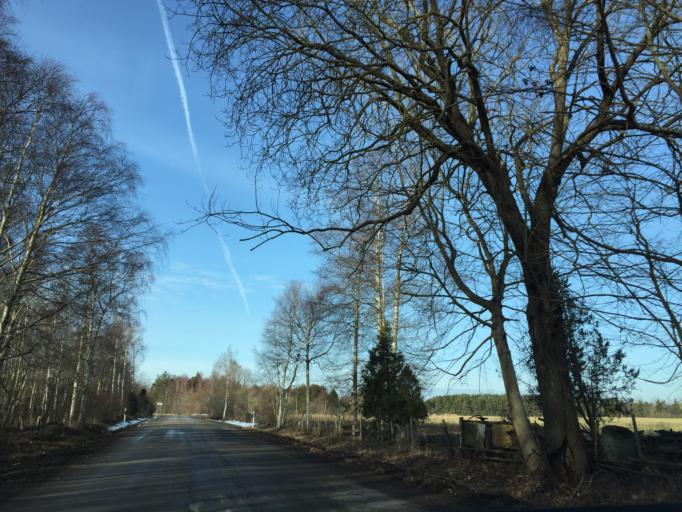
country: EE
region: Saare
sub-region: Kuressaare linn
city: Kuressaare
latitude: 58.3663
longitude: 22.0325
